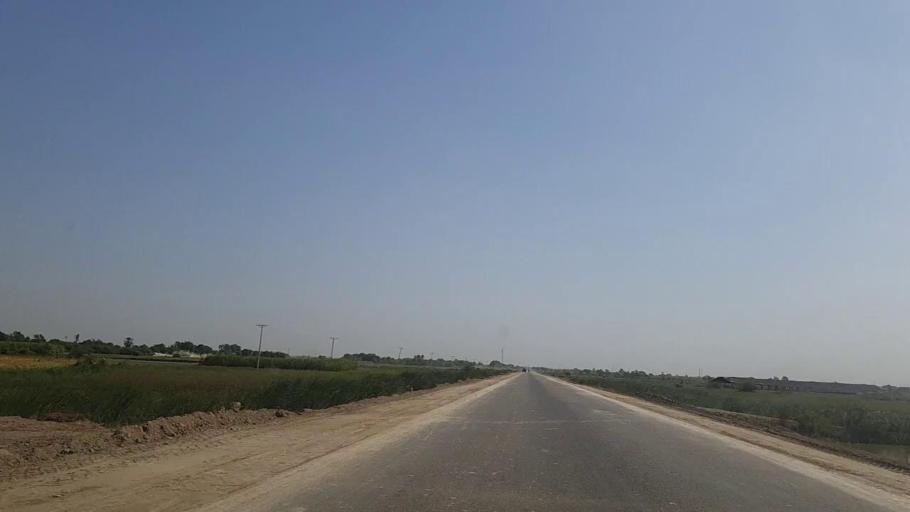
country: PK
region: Sindh
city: Mirpur Batoro
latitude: 24.7487
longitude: 68.2382
